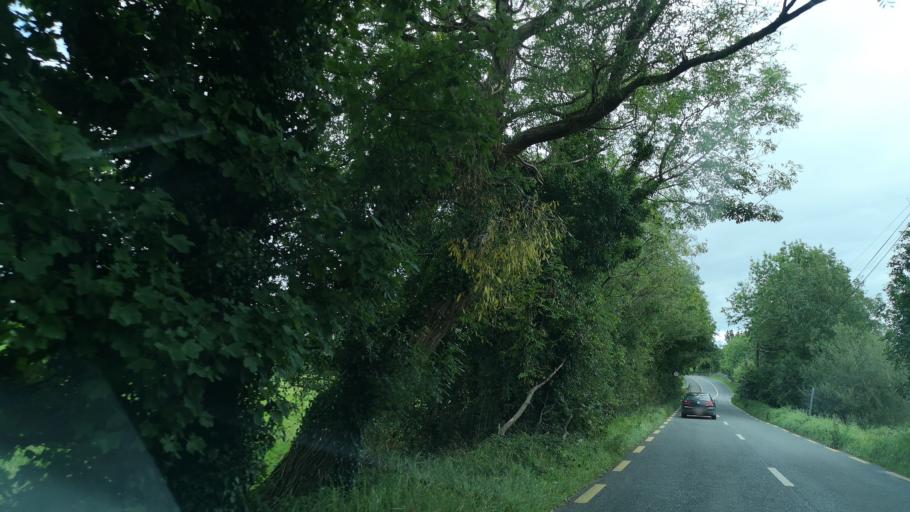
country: IE
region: Leinster
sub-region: Uibh Fhaili
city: Banagher
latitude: 53.2796
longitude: -8.0632
